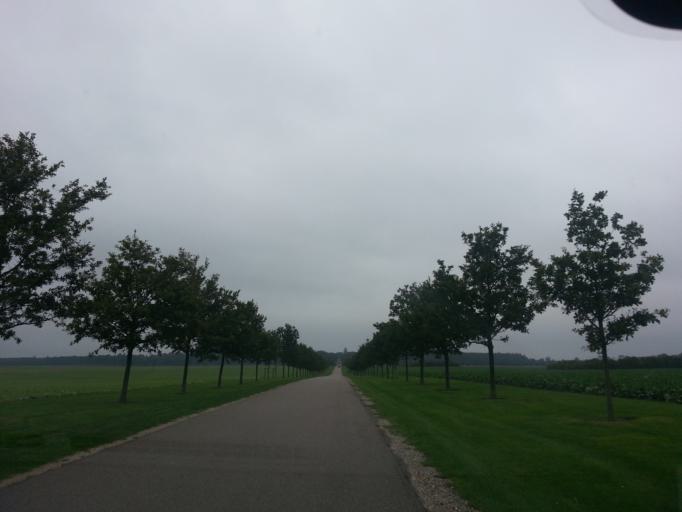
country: DK
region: Zealand
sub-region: Lolland Kommune
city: Maribo
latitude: 54.8016
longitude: 11.5074
